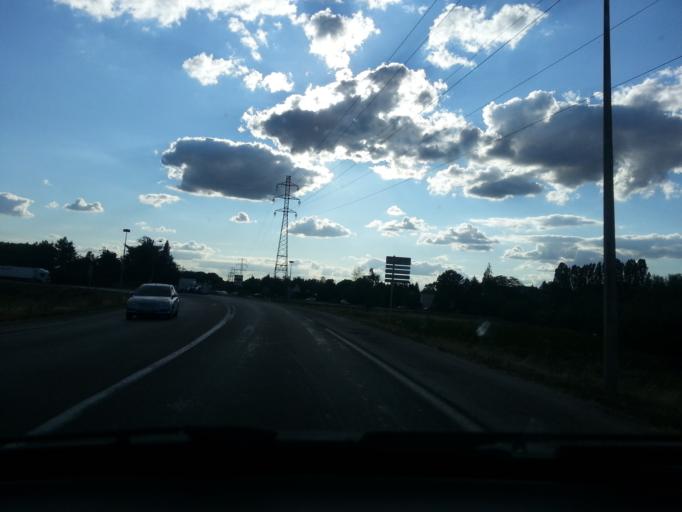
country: FR
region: Bourgogne
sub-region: Departement de Saone-et-Loire
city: Saint-Remy
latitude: 46.7590
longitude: 4.8457
